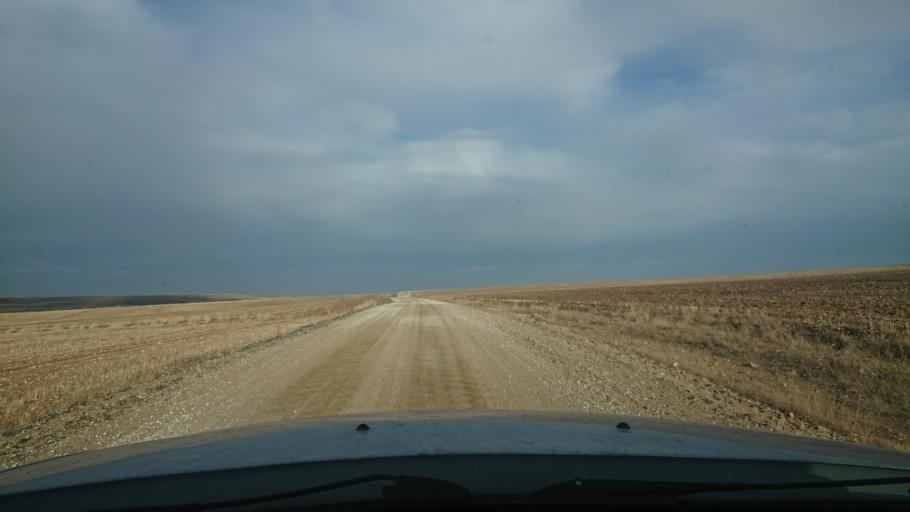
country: TR
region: Aksaray
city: Ortakoy
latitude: 38.7054
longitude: 33.8710
